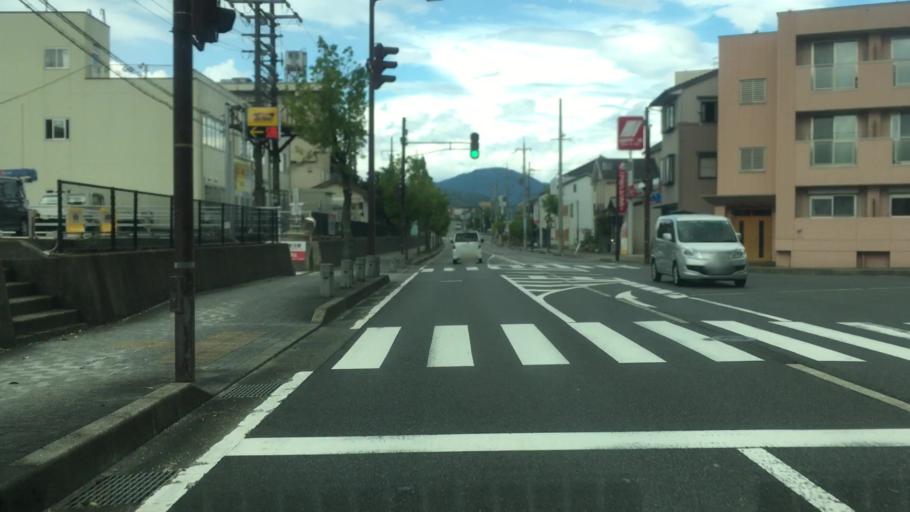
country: JP
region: Hyogo
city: Toyooka
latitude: 35.5447
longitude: 134.8141
